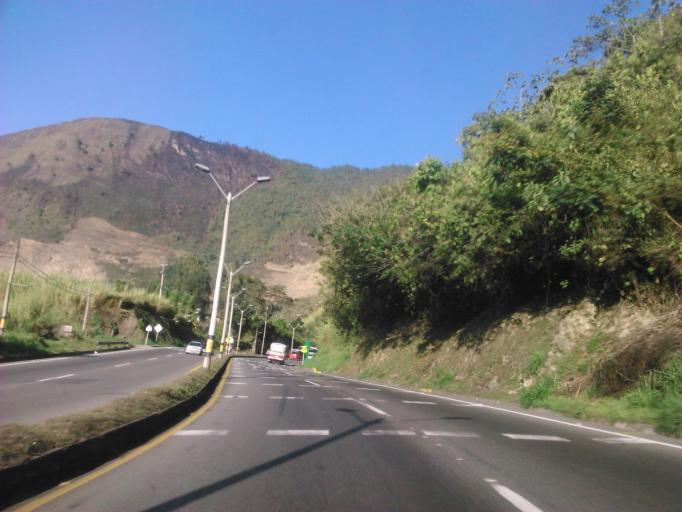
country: CO
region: Antioquia
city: Municipio de Copacabana
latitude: 6.3143
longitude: -75.4954
